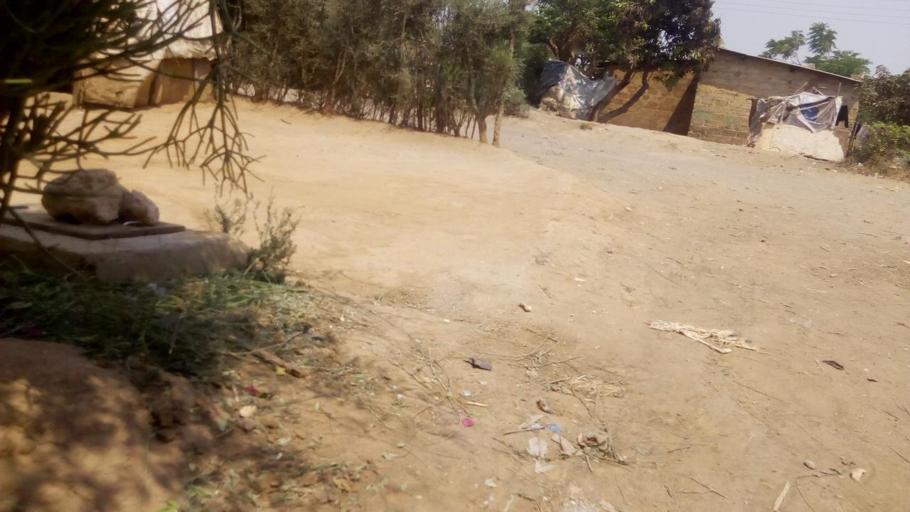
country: ZM
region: Lusaka
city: Lusaka
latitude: -15.3536
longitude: 28.2904
